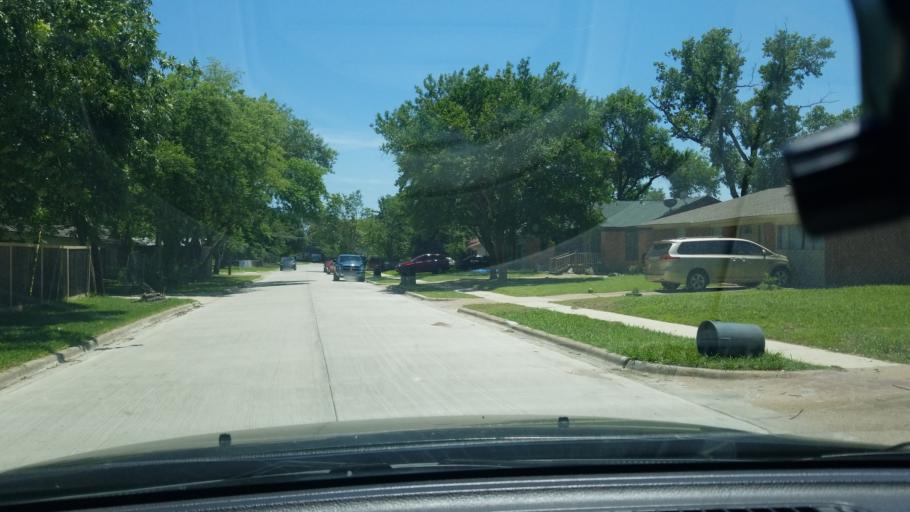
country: US
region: Texas
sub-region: Dallas County
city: Mesquite
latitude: 32.7724
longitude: -96.6052
